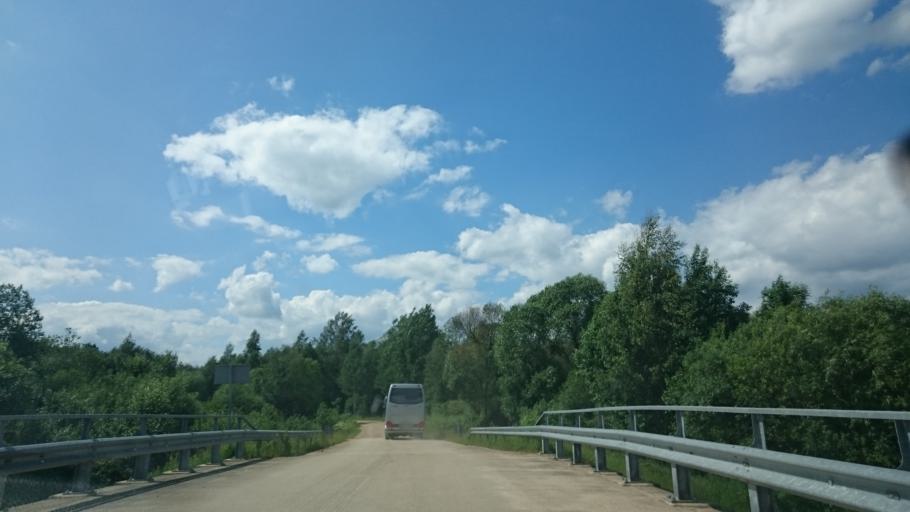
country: LV
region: Cibla
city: Cibla
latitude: 56.6223
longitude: 27.9230
